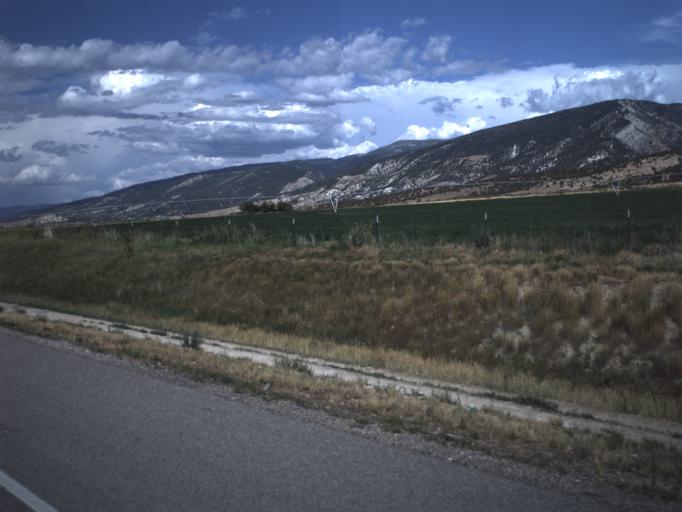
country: US
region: Utah
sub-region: Sanpete County
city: Manti
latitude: 39.3090
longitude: -111.6131
